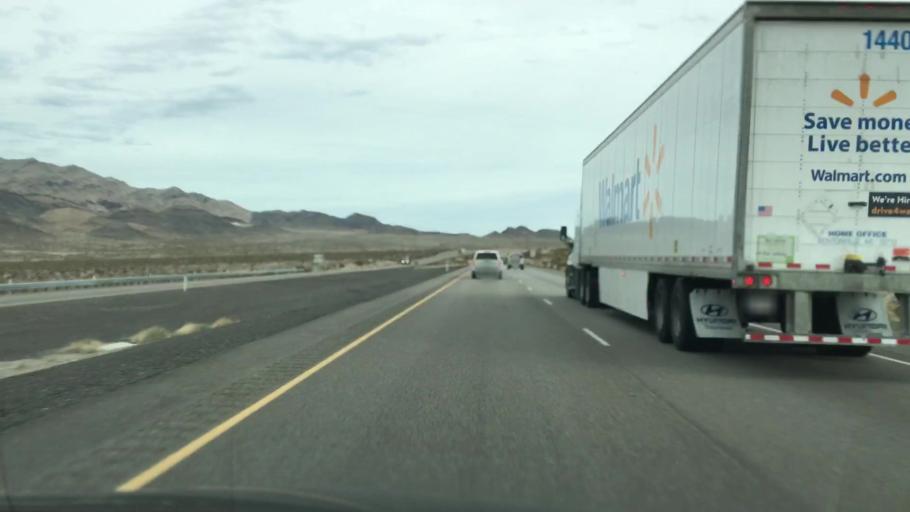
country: US
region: Nevada
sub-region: Nye County
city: Pahrump
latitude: 36.6000
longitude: -115.9867
